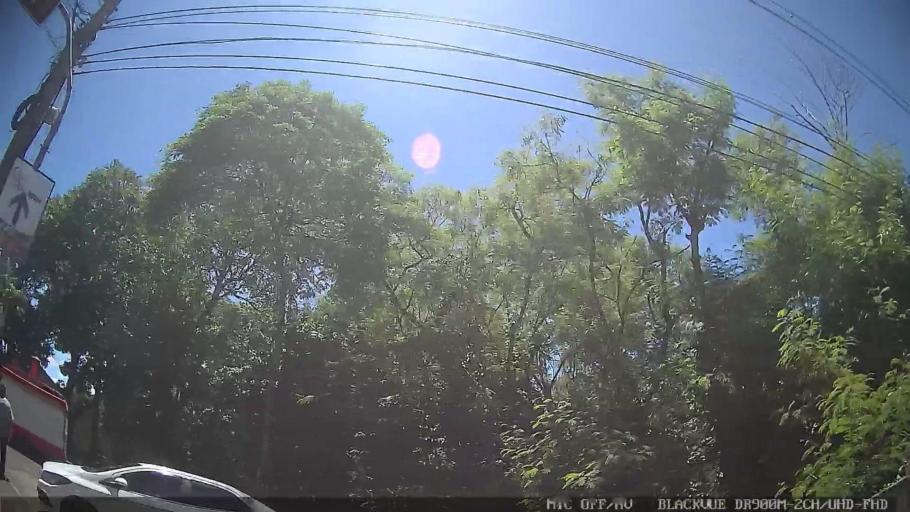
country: BR
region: Sao Paulo
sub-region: Pedreira
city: Pedreira
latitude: -22.7422
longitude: -46.9097
